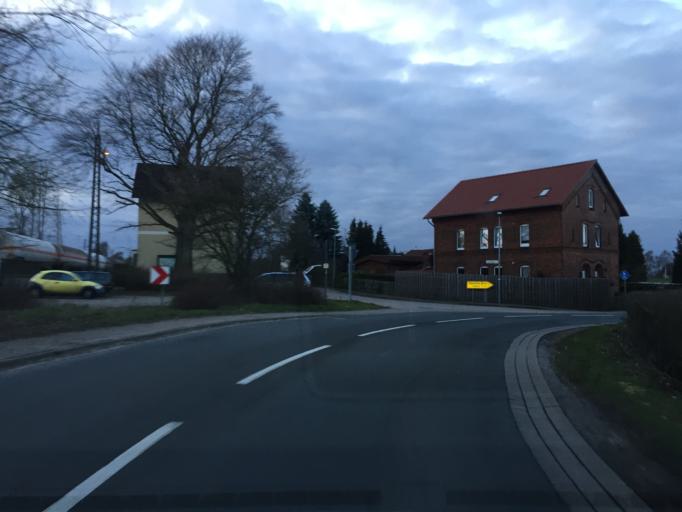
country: DE
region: Lower Saxony
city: Steimbke
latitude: 52.5771
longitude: 9.4043
